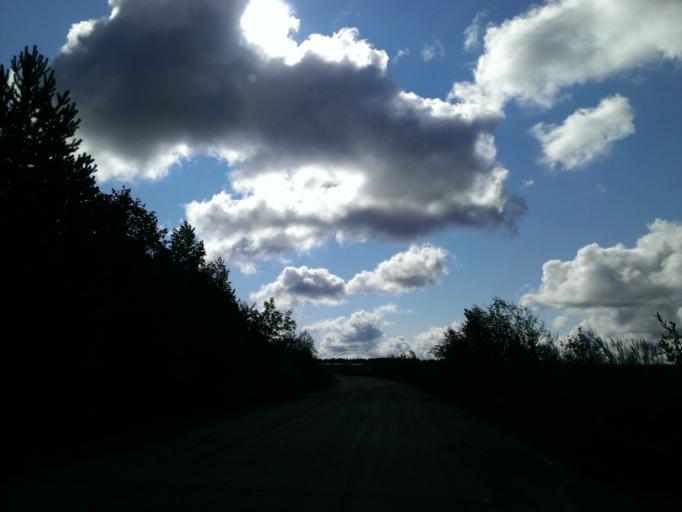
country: LV
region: Incukalns
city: Vangazi
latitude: 57.0920
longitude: 24.5068
